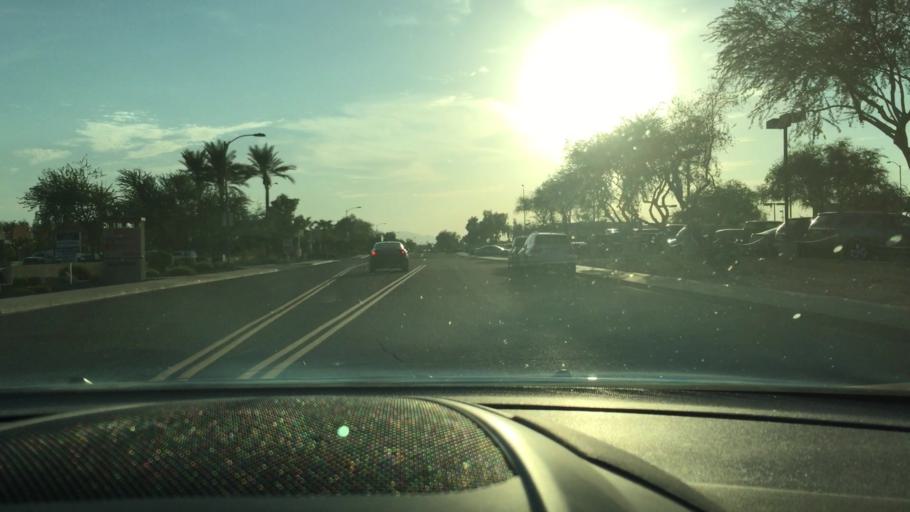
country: US
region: Arizona
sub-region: Maricopa County
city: Sun City
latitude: 33.6354
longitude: -112.2451
